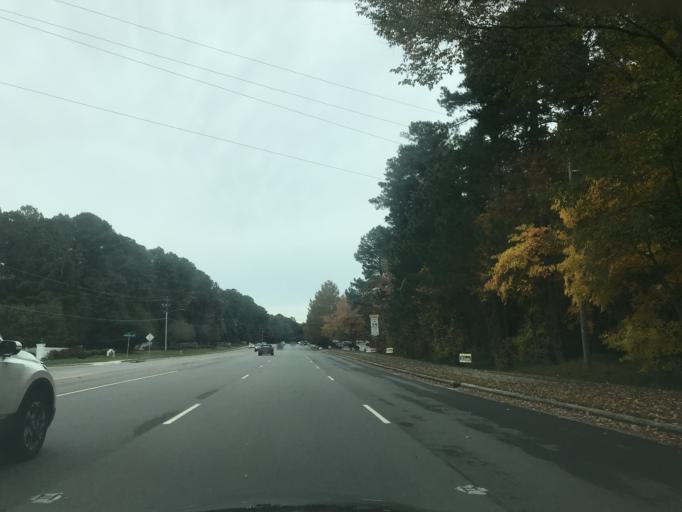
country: US
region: North Carolina
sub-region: Wake County
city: West Raleigh
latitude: 35.8942
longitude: -78.6332
